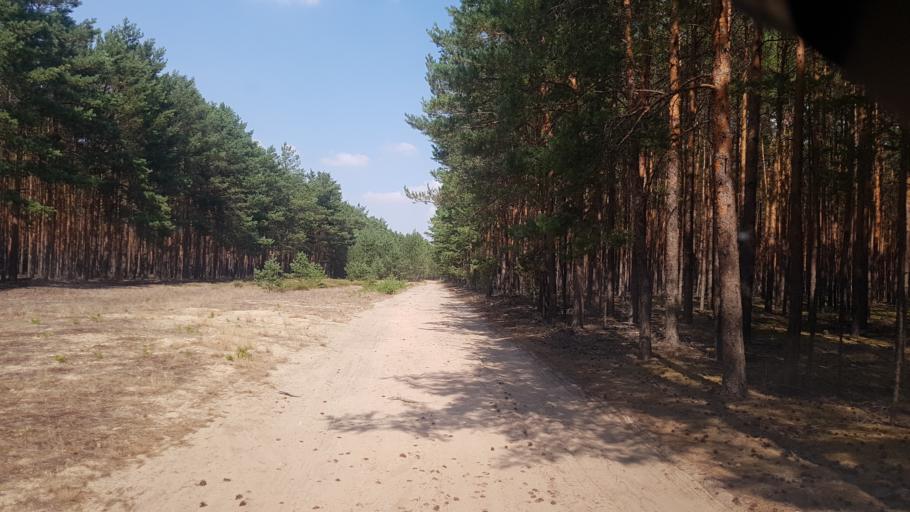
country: DE
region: Brandenburg
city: Spremberg
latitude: 51.6370
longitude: 14.4083
